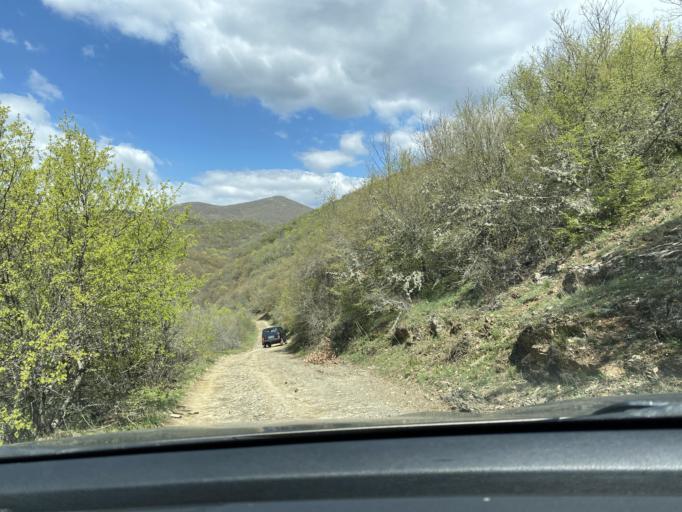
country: MK
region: Caska
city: Caska
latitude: 41.7346
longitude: 21.6490
